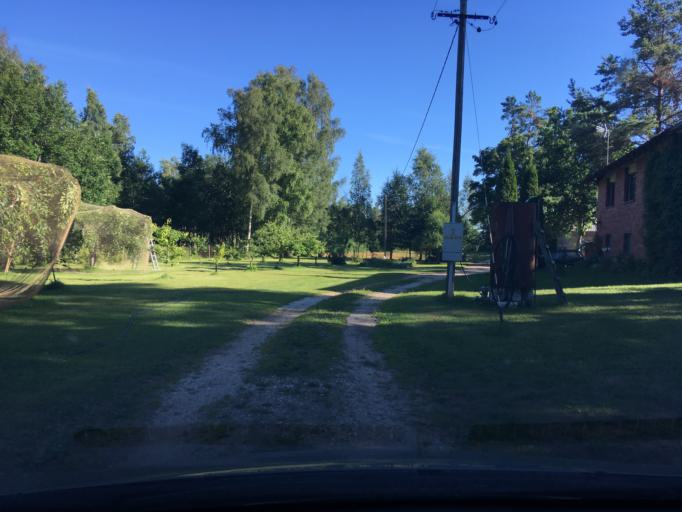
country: EE
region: Laeaene
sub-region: Lihula vald
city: Lihula
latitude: 58.5857
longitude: 23.7362
